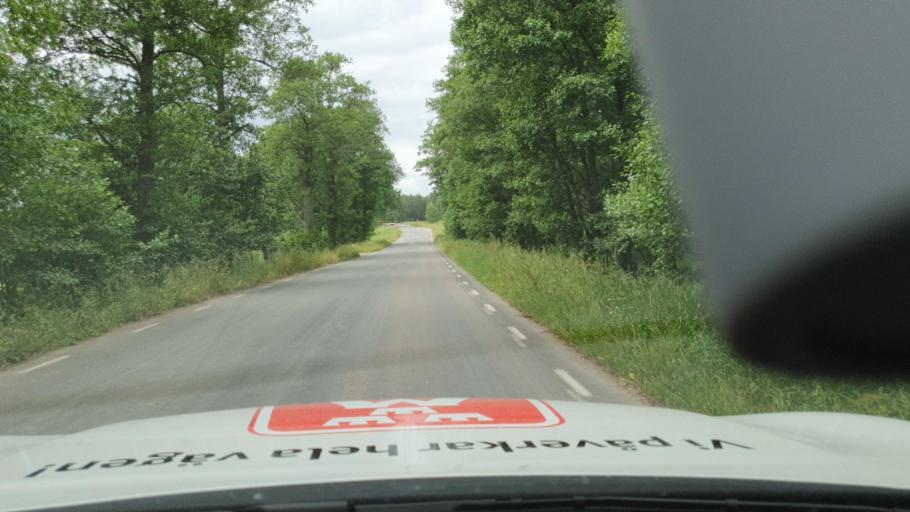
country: SE
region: Vaestra Goetaland
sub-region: Tidaholms Kommun
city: Olofstorp
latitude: 58.1925
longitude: 14.0330
